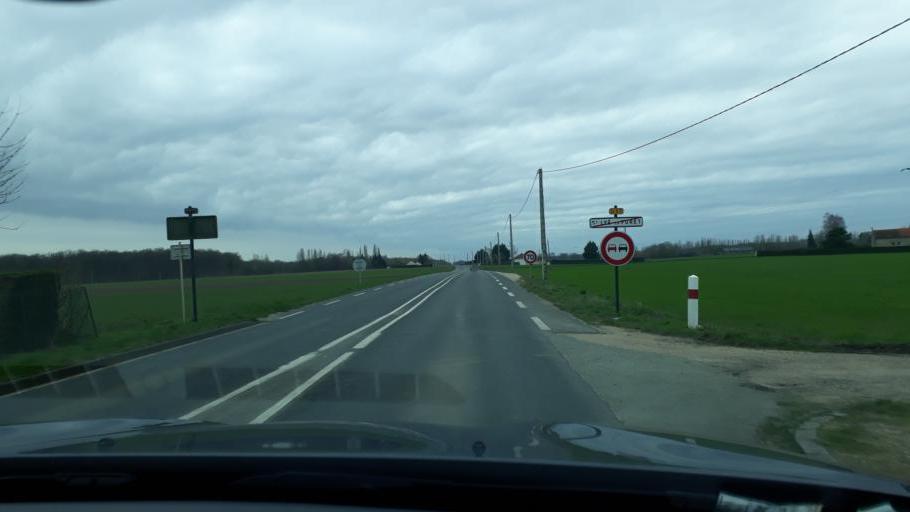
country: FR
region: Centre
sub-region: Departement du Loiret
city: Chanteau
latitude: 48.0353
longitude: 1.9772
